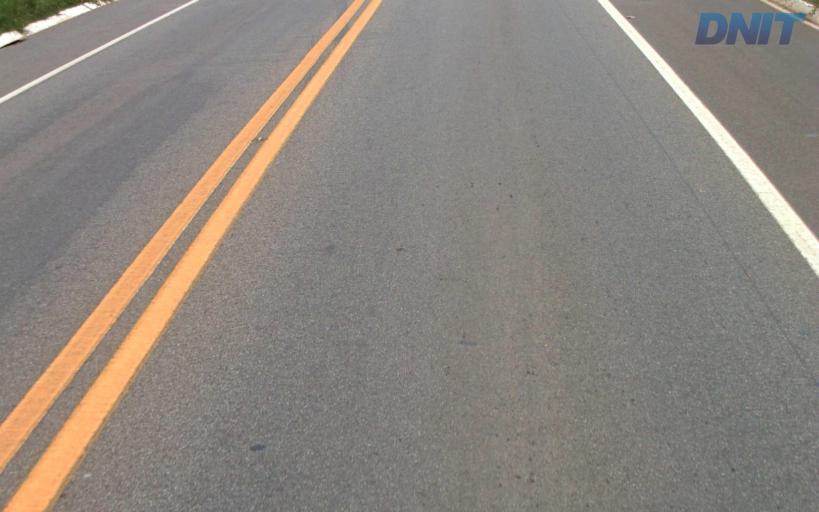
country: BR
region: Minas Gerais
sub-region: Governador Valadares
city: Governador Valadares
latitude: -18.8512
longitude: -41.9836
